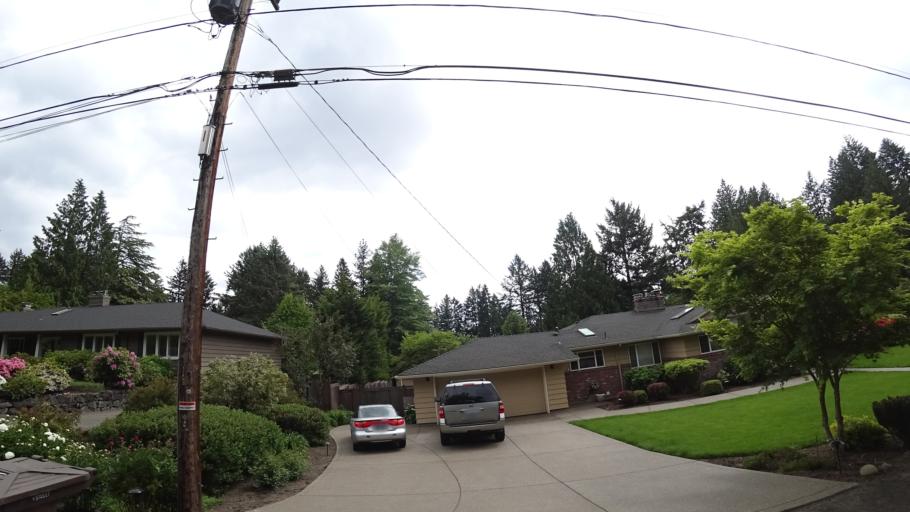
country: US
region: Oregon
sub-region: Washington County
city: West Slope
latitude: 45.4991
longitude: -122.7818
